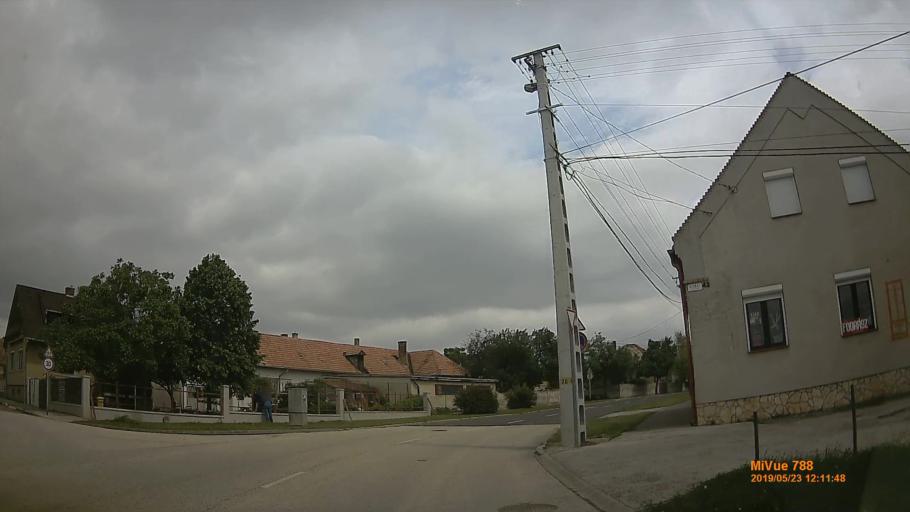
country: HU
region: Veszprem
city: Veszprem
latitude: 47.1034
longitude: 17.8964
